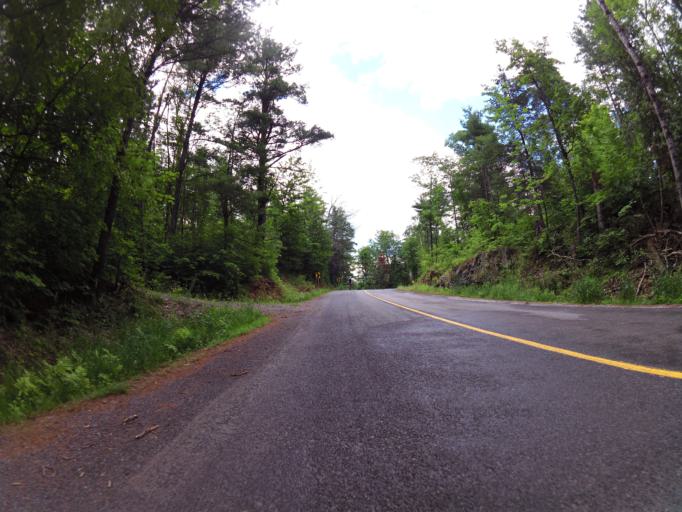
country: CA
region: Ontario
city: Renfrew
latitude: 45.0476
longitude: -76.6958
